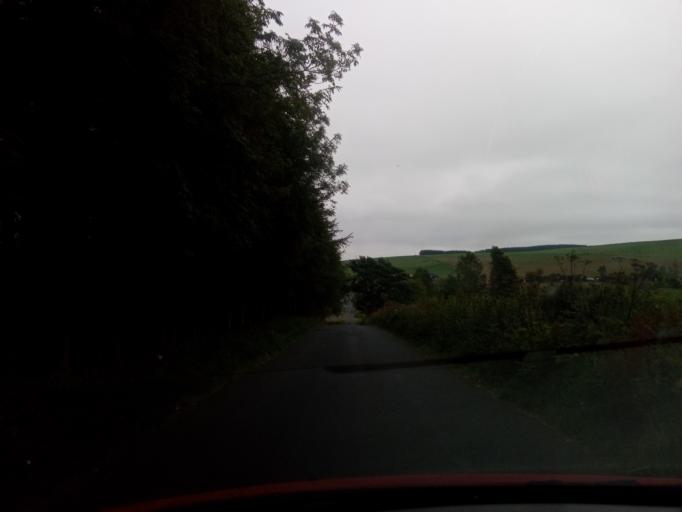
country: GB
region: Scotland
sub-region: Fife
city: Pathhead
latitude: 55.7371
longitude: -2.9140
